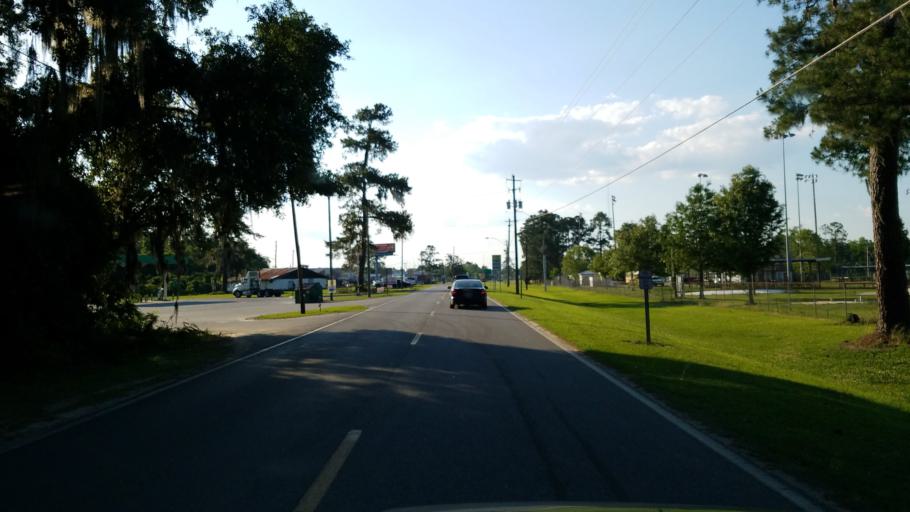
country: US
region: Georgia
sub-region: Lanier County
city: Lakeland
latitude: 31.0315
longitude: -83.0706
